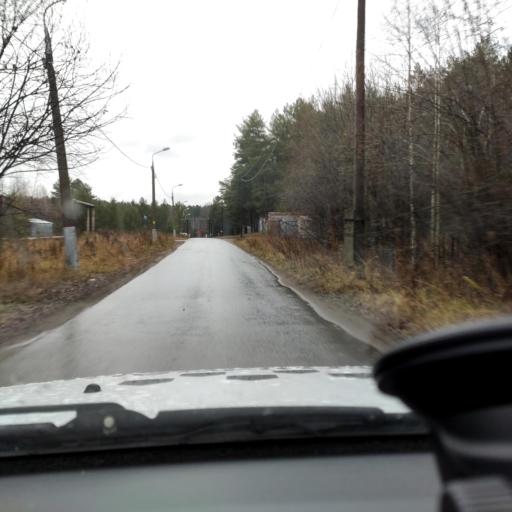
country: RU
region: Perm
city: Perm
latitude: 58.0559
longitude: 56.2814
